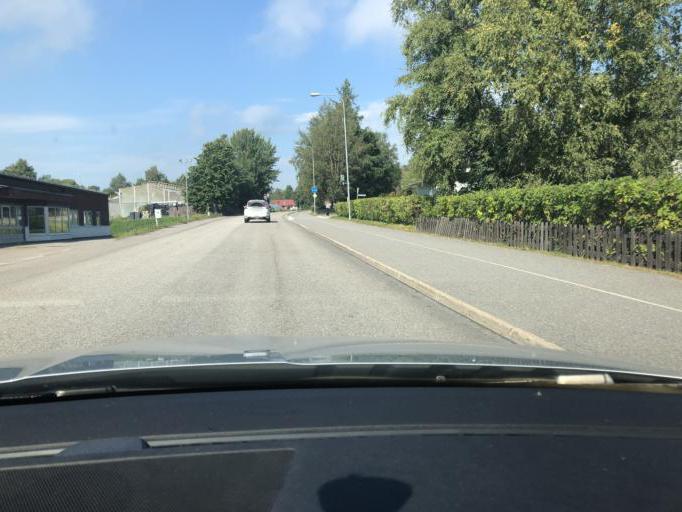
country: SE
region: Vaesternorrland
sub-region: Haernoesands Kommun
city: Haernoesand
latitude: 62.6409
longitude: 17.9162
